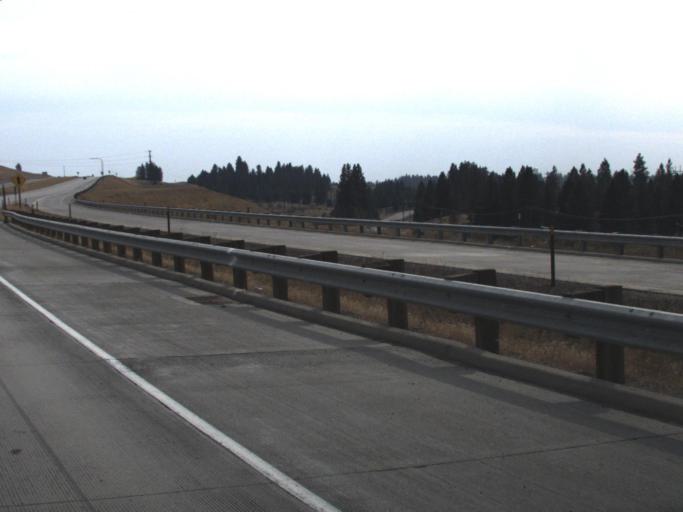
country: US
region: Washington
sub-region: Spokane County
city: Mead
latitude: 47.7513
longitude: -117.3597
